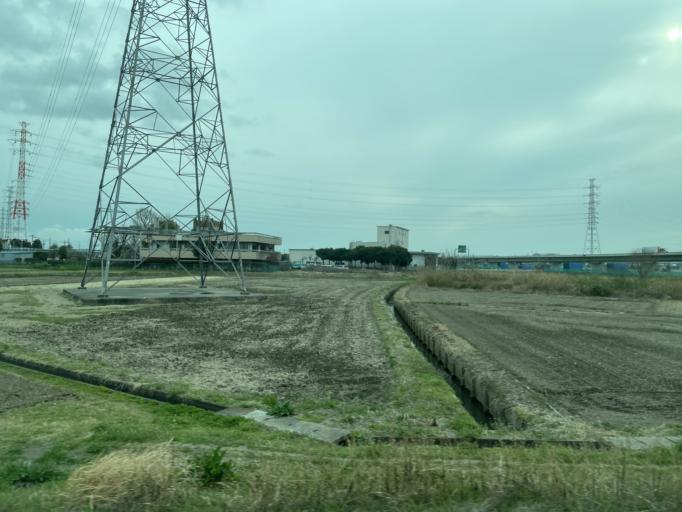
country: JP
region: Saitama
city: Kukichuo
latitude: 36.0498
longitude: 139.6877
